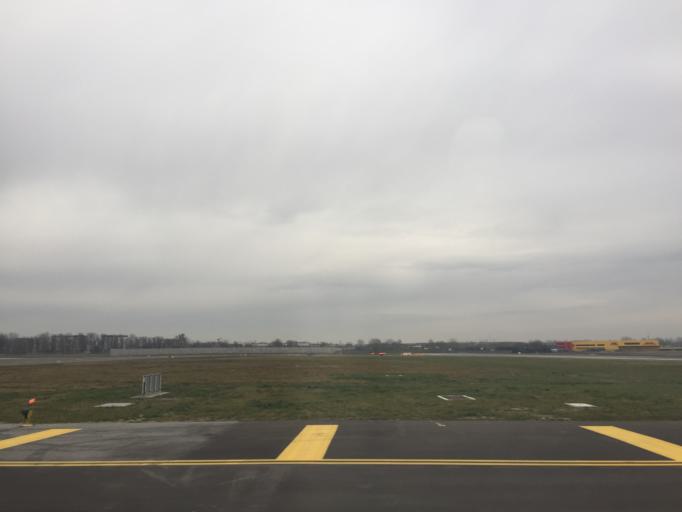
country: PL
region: Masovian Voivodeship
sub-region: Warszawa
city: Wlochy
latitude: 52.1637
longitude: 20.9776
